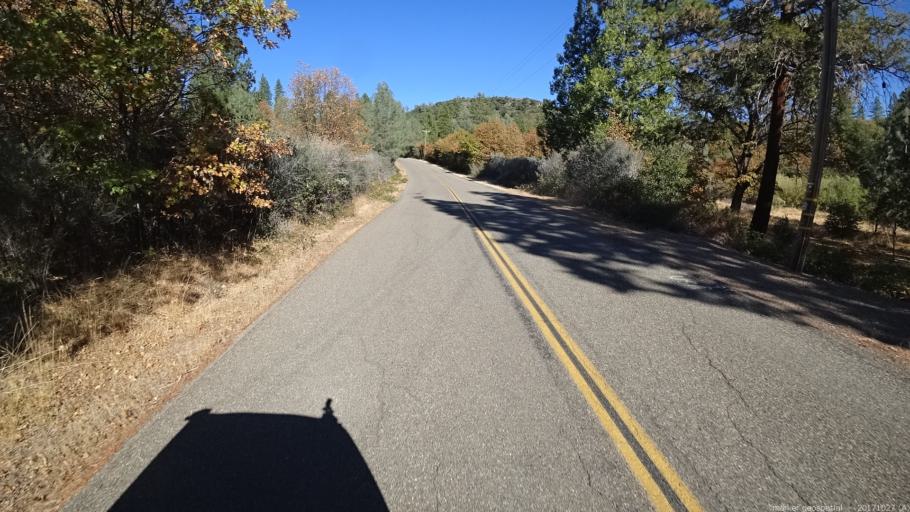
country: US
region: California
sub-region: Shasta County
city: Shingletown
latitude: 40.6513
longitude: -121.8802
